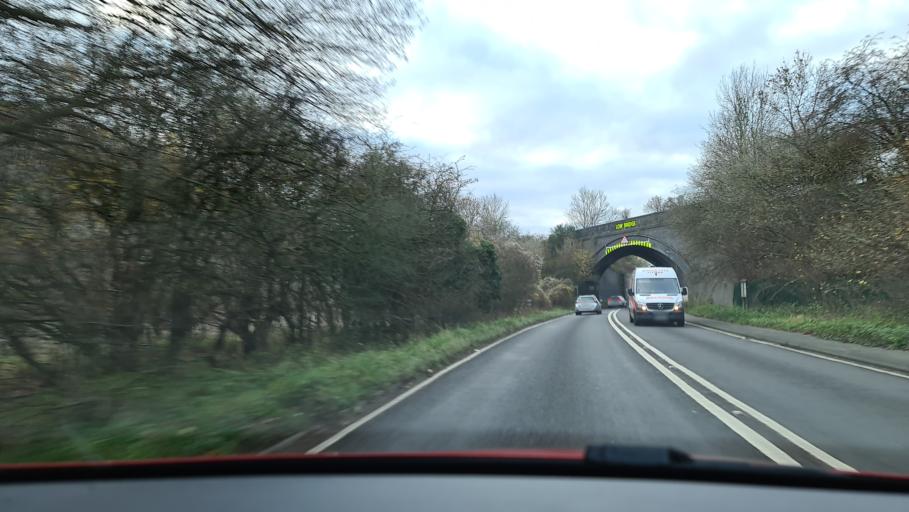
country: GB
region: England
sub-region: Buckinghamshire
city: High Wycombe
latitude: 51.6550
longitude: -0.8004
